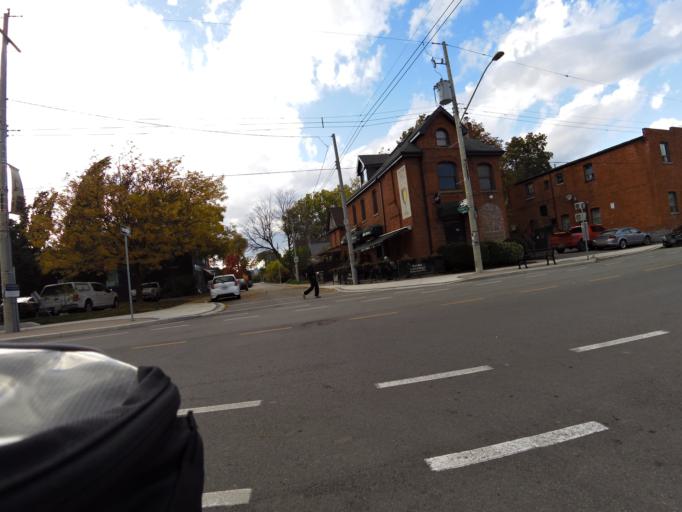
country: CA
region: Ontario
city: Hamilton
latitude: 43.2580
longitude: -79.8844
